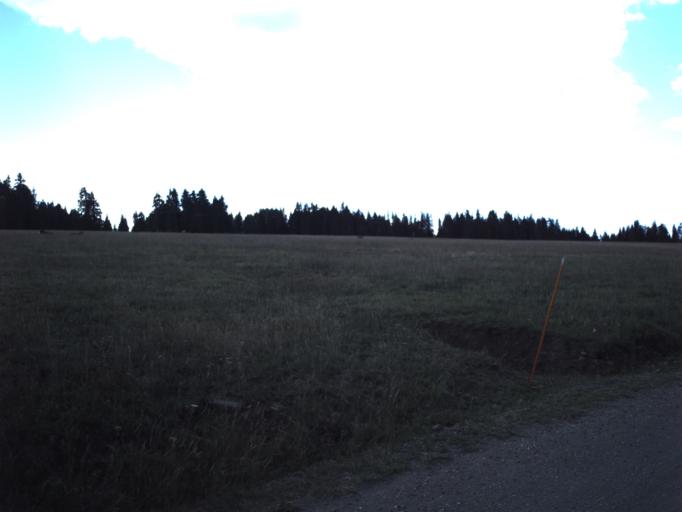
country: US
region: Utah
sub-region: Piute County
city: Junction
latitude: 38.2804
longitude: -112.3610
